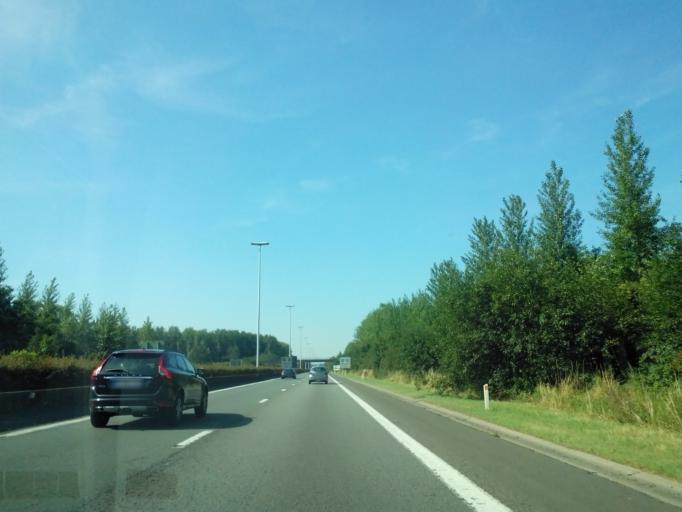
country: BE
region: Flanders
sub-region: Provincie Vlaams-Brabant
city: Holsbeek
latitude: 50.9237
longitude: 4.7336
